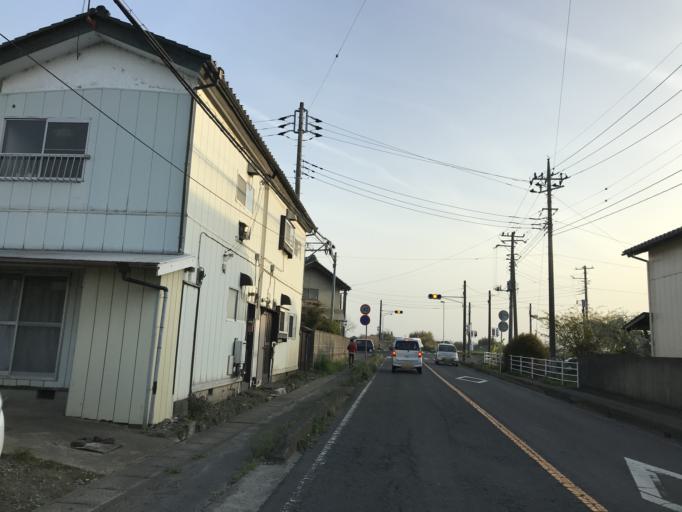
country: JP
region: Ibaraki
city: Katsuta
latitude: 36.3726
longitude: 140.5188
